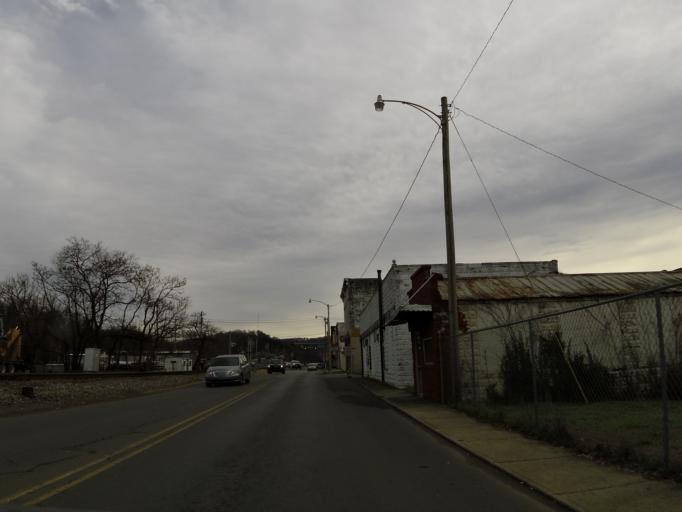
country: US
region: Tennessee
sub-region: Cocke County
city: Newport
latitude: 35.9678
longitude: -83.1889
